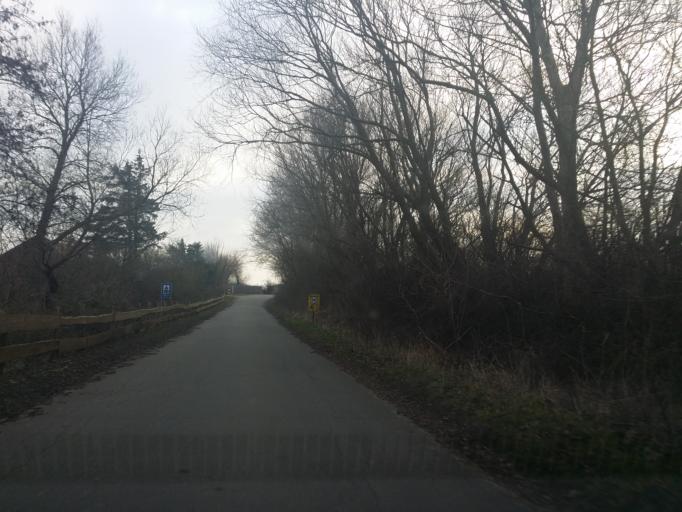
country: DE
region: Schleswig-Holstein
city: Heiligenhafen
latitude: 54.4538
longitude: 11.0129
